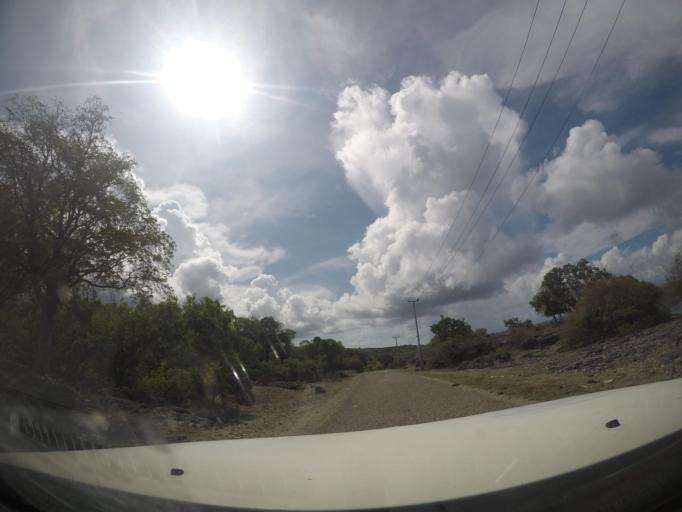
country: TL
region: Lautem
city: Lospalos
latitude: -8.3442
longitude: 127.0454
